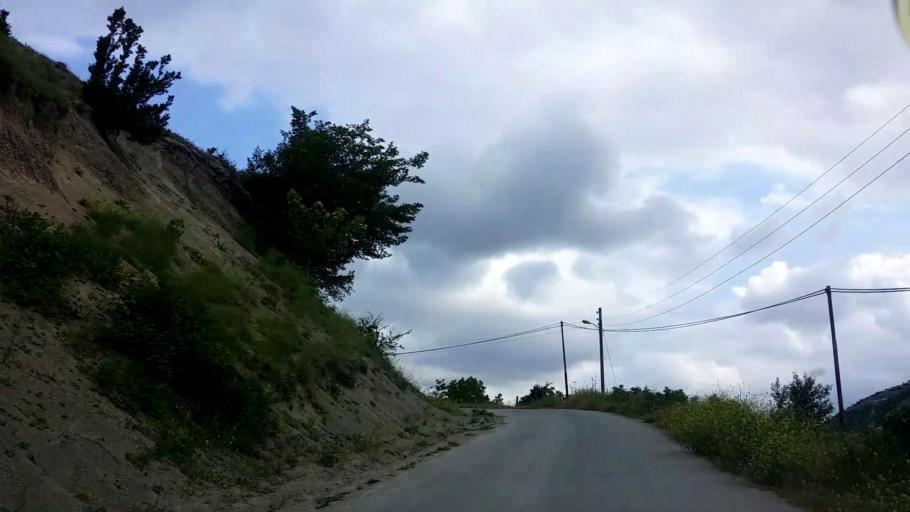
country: IR
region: Mazandaran
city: Chalus
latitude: 36.5550
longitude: 51.2764
